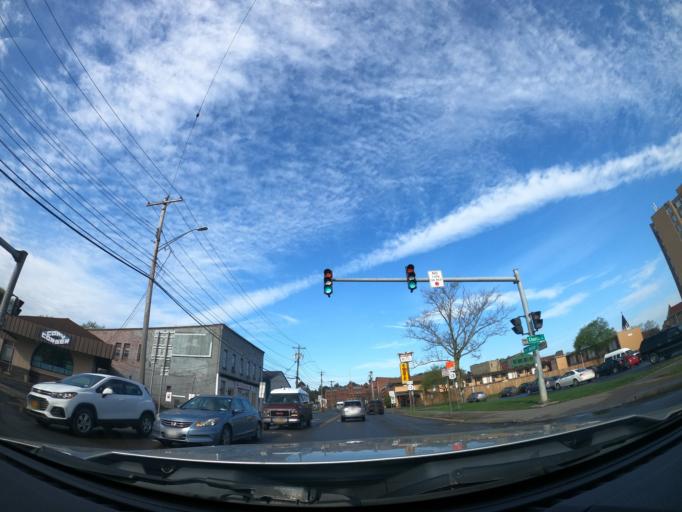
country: US
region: New York
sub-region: Cortland County
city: Cortland
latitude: 42.5978
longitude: -76.1779
